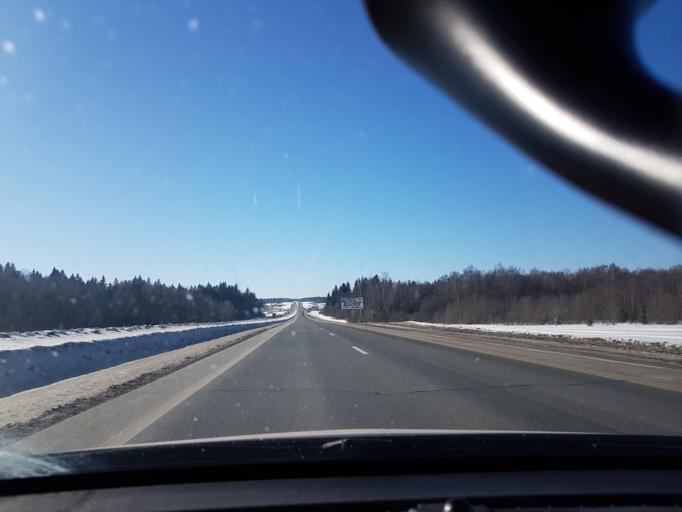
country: RU
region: Moskovskaya
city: Sychevo
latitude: 55.9915
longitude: 36.2567
